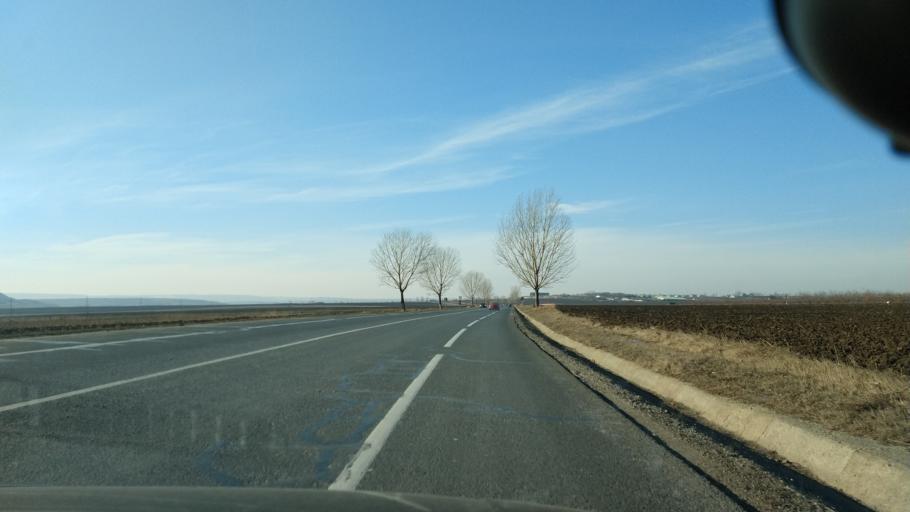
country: RO
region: Iasi
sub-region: Comuna Ion Neculce
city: Razboieni
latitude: 47.2206
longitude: 27.0959
